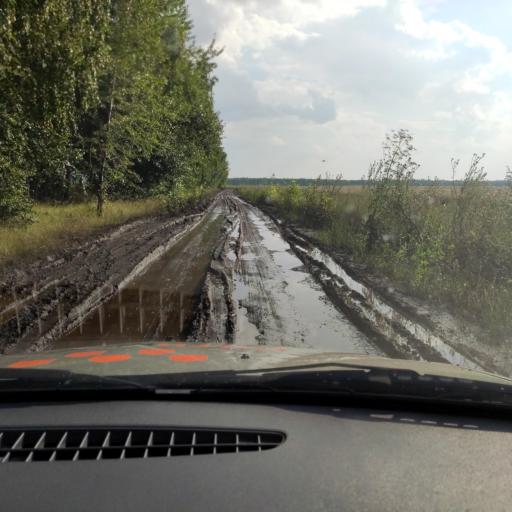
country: RU
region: Bashkortostan
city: Avdon
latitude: 54.5554
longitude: 55.8224
